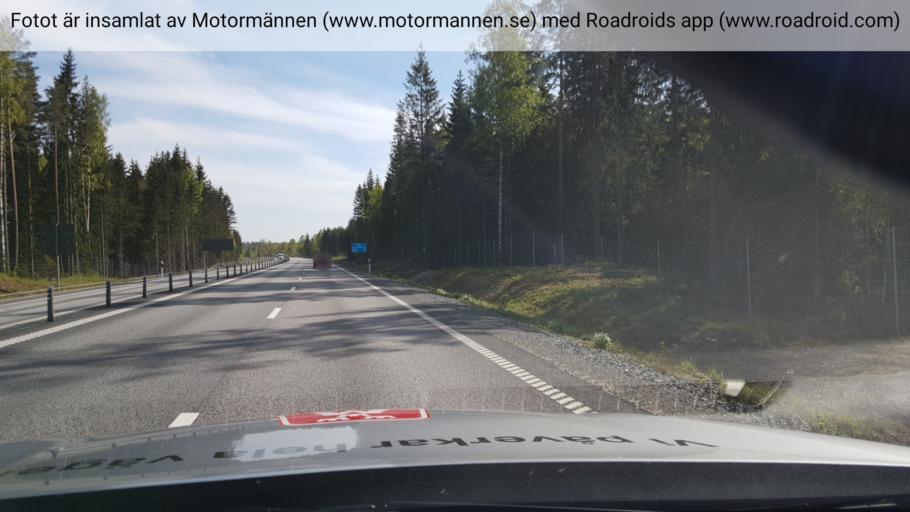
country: SE
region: Uppsala
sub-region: Heby Kommun
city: Heby
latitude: 60.0150
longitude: 16.8554
